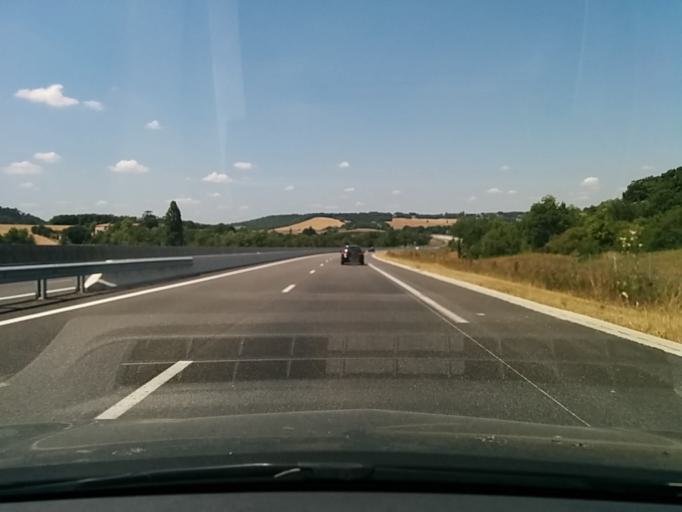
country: FR
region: Midi-Pyrenees
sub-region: Departement du Gers
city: Preignan
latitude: 43.6537
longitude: 0.6675
